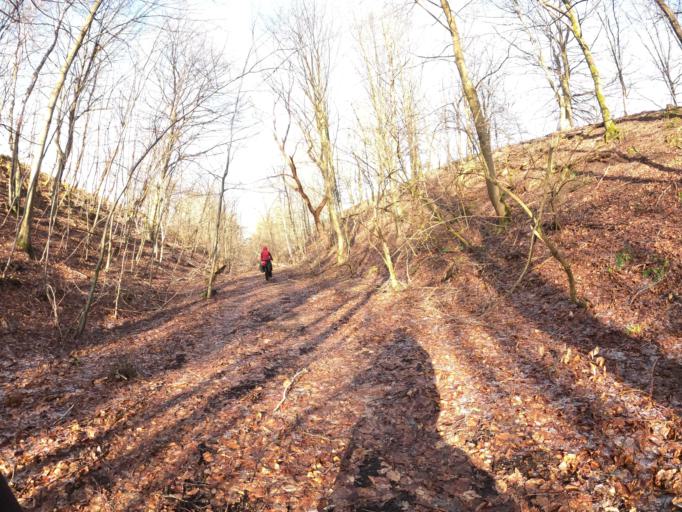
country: PL
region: West Pomeranian Voivodeship
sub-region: Powiat koszalinski
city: Polanow
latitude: 54.1380
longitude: 16.7721
